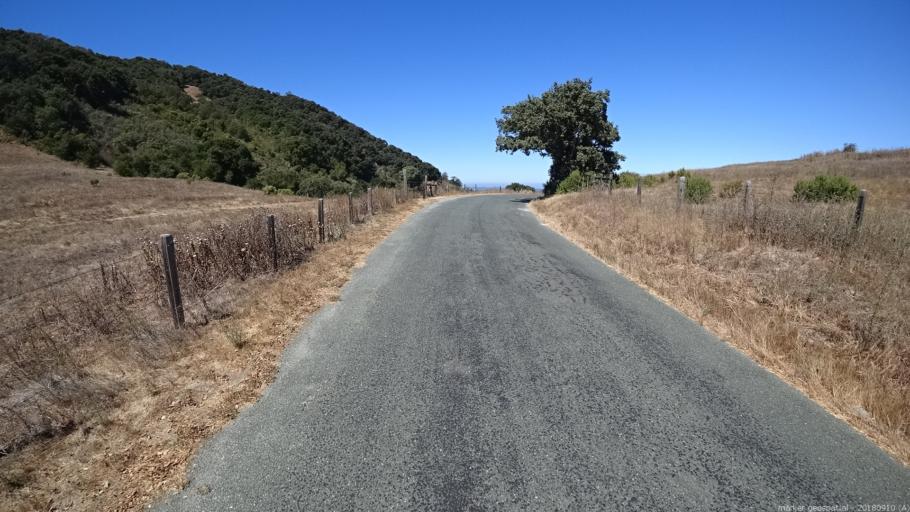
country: US
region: California
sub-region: Monterey County
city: Carmel Valley Village
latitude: 36.4707
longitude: -121.8021
